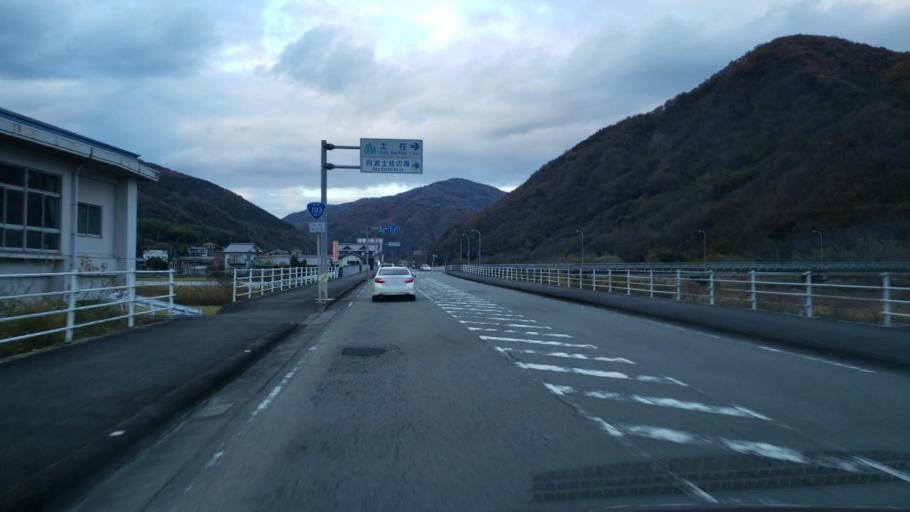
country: JP
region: Tokushima
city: Wakimachi
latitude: 34.0895
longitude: 134.1730
